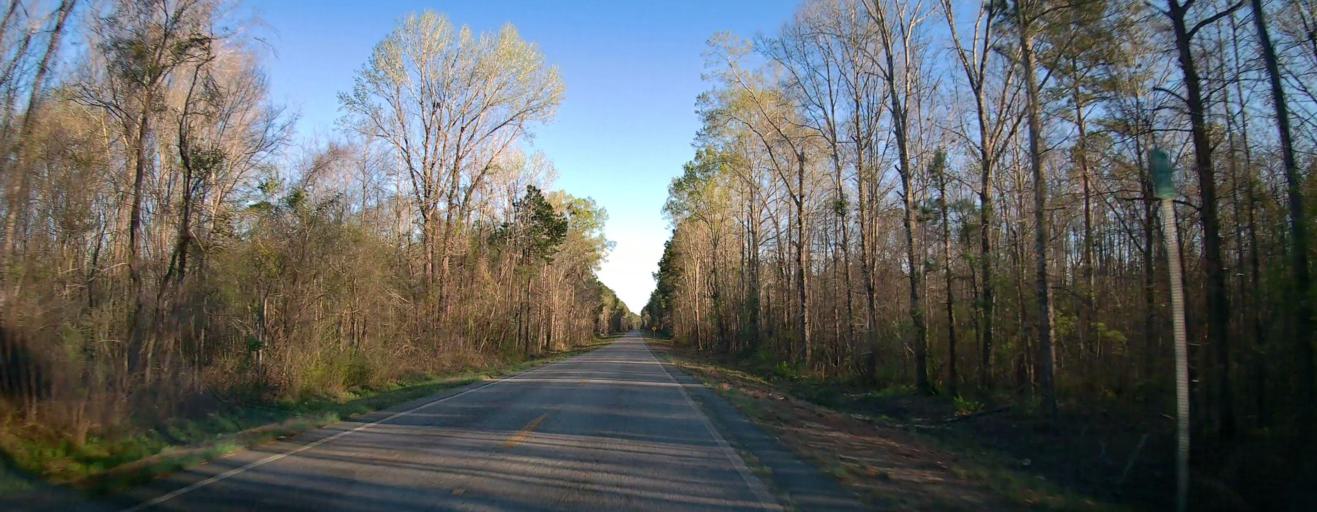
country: US
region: Georgia
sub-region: Wilcox County
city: Abbeville
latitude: 32.0970
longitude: -83.3009
